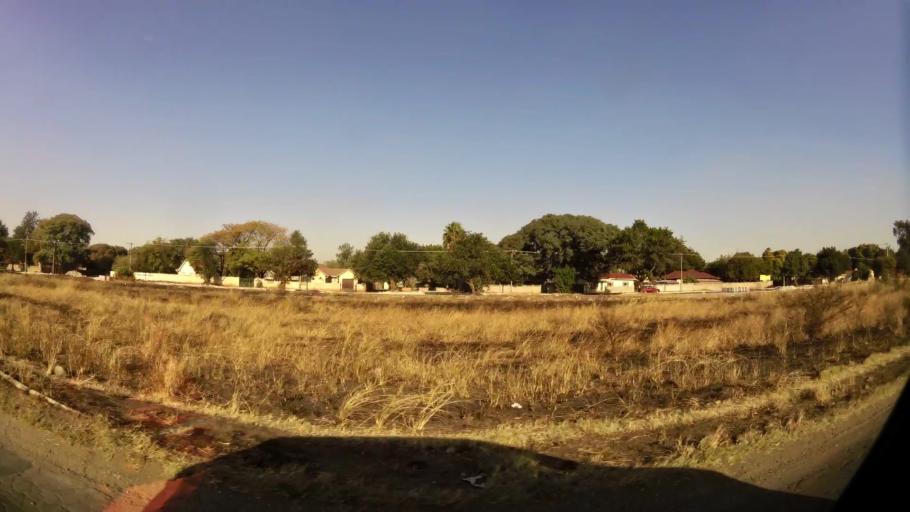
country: ZA
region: North-West
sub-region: Bojanala Platinum District Municipality
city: Rustenburg
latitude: -25.6465
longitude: 27.2274
